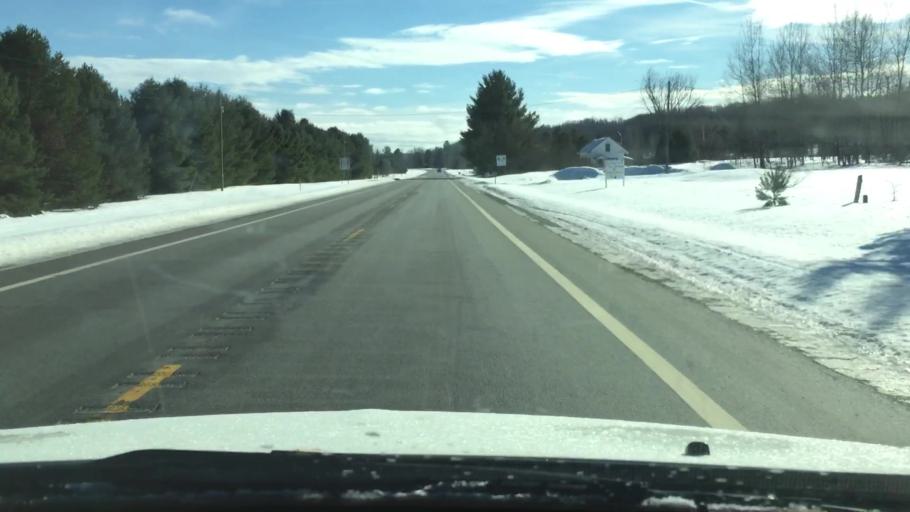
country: US
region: Michigan
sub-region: Charlevoix County
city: East Jordan
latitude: 45.0738
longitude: -85.0868
